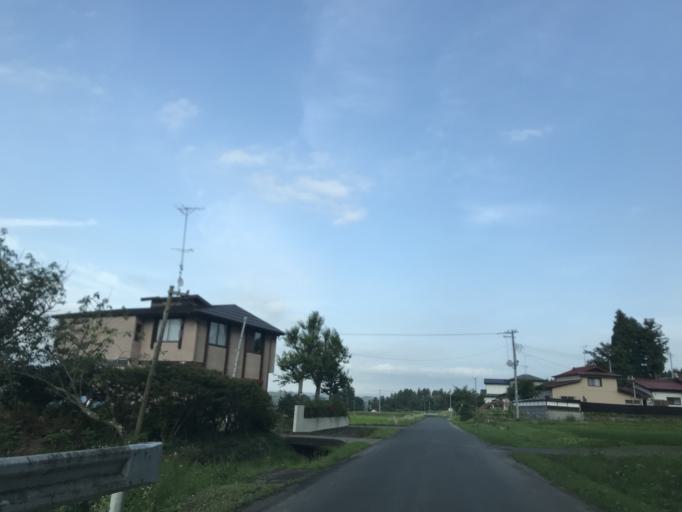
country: JP
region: Iwate
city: Ichinoseki
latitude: 38.8397
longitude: 141.1651
